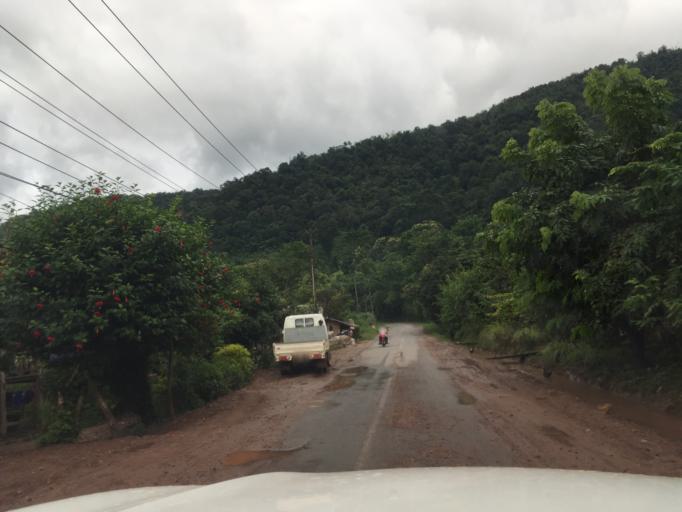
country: LA
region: Oudomxai
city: Muang La
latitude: 20.7874
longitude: 102.0740
